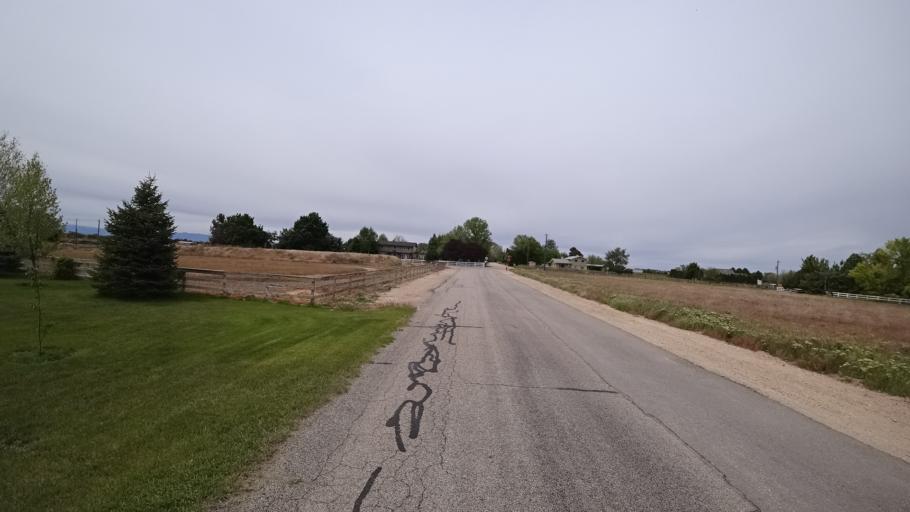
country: US
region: Idaho
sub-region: Ada County
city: Meridian
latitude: 43.5548
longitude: -116.3735
